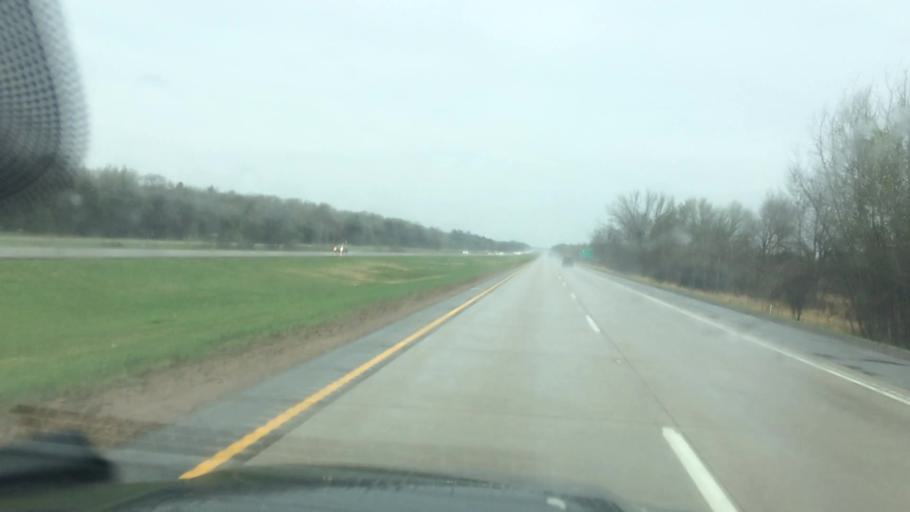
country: US
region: Wisconsin
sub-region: Portage County
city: Stevens Point
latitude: 44.6187
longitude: -89.6276
